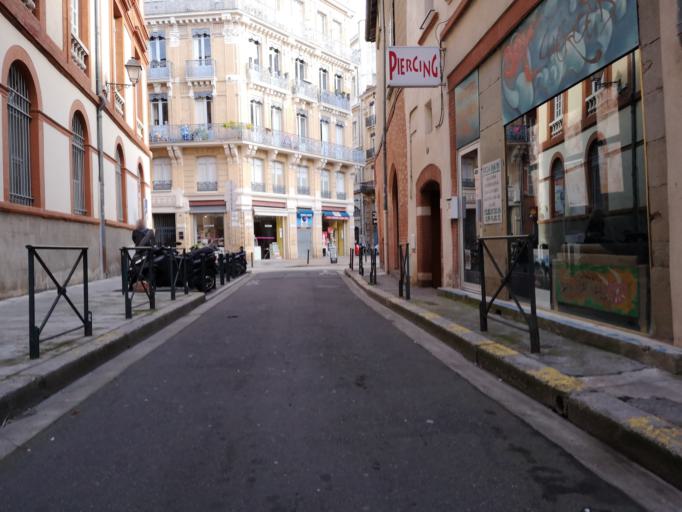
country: FR
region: Midi-Pyrenees
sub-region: Departement de la Haute-Garonne
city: Toulouse
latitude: 43.6058
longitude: 1.4440
